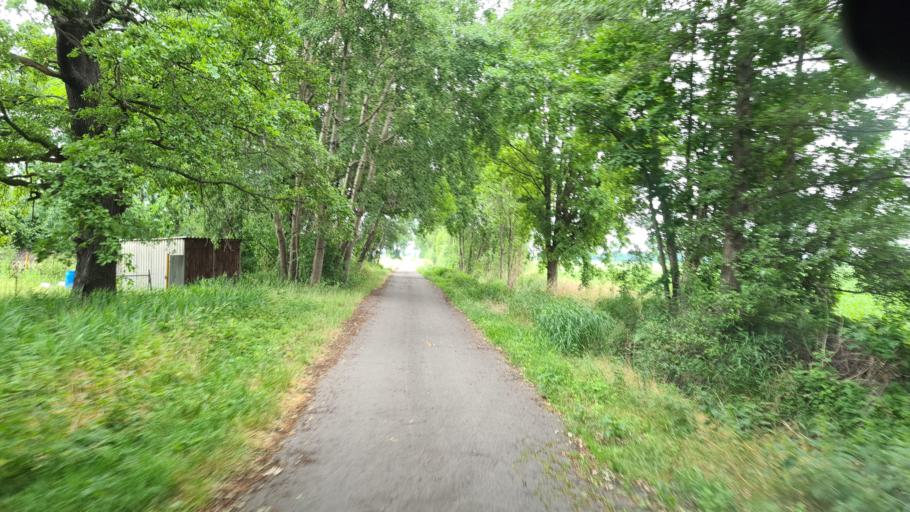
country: DE
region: Brandenburg
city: Groden
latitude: 51.4086
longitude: 13.5794
